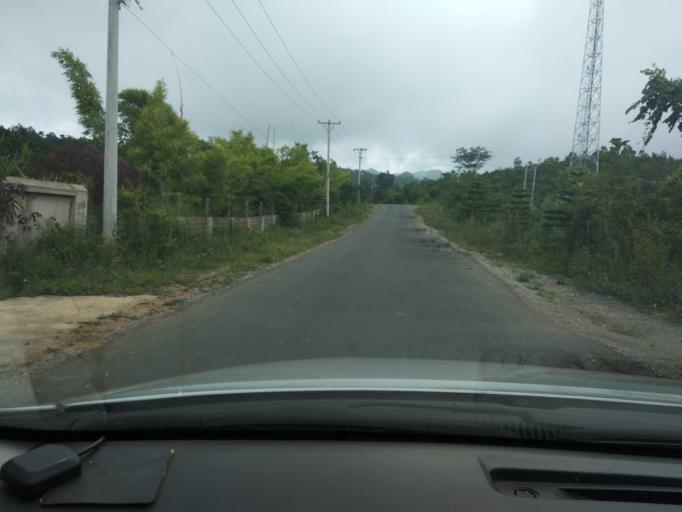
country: MM
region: Mandalay
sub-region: Pyin Oo Lwin District
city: Pyin Oo Lwin
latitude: 21.9214
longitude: 96.3777
